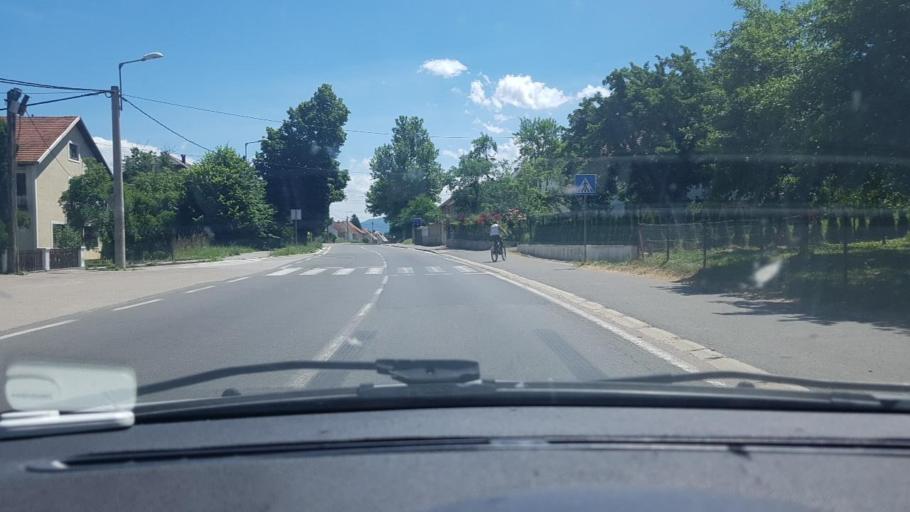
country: HR
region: Licko-Senjska
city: Otocac
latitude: 44.8686
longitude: 15.2456
